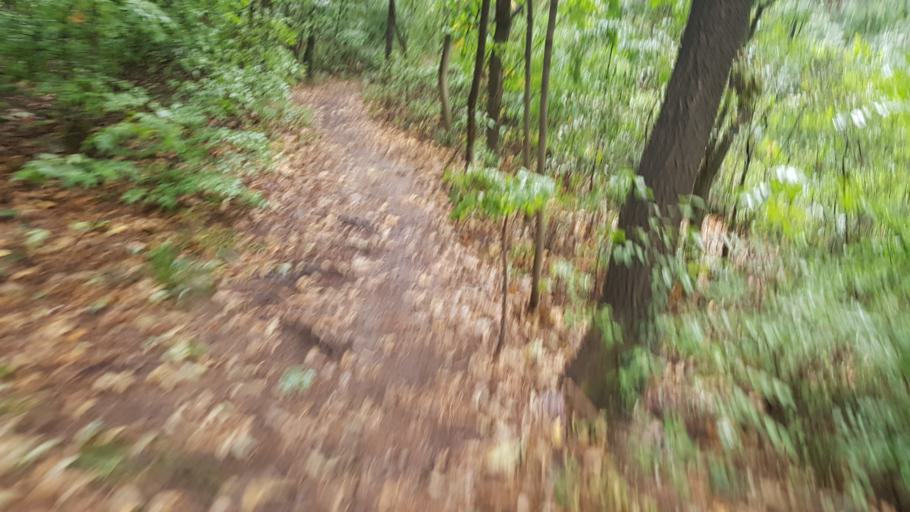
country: HU
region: Pest
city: Toeroekbalint
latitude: 47.4659
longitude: 18.9205
